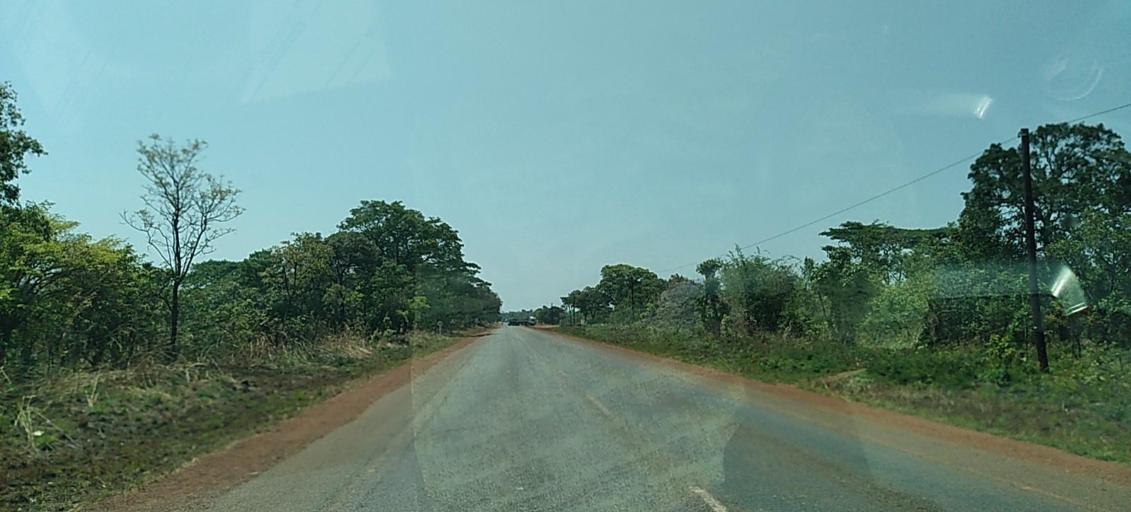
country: ZM
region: North-Western
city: Solwezi
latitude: -12.3556
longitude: 25.9273
